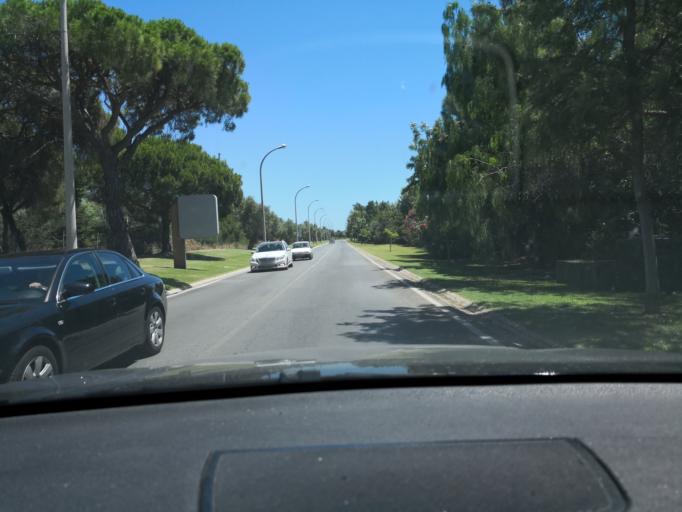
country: PT
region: Faro
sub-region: Loule
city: Vilamoura
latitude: 37.1054
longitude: -8.1346
